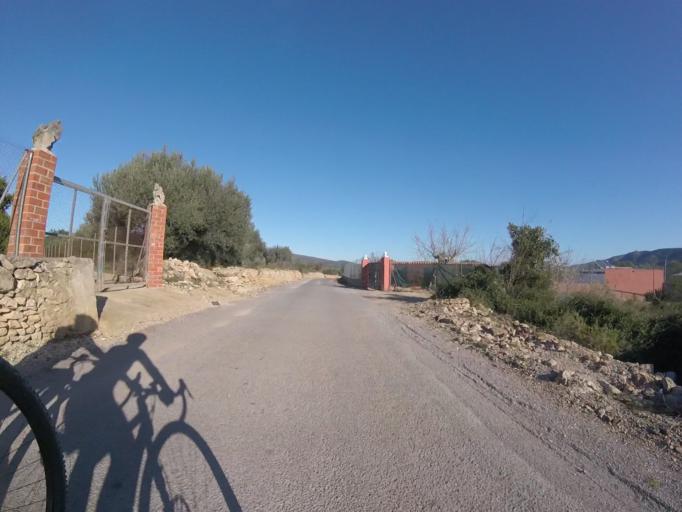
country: ES
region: Valencia
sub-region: Provincia de Castello
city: Alcala de Xivert
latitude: 40.2913
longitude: 0.2167
